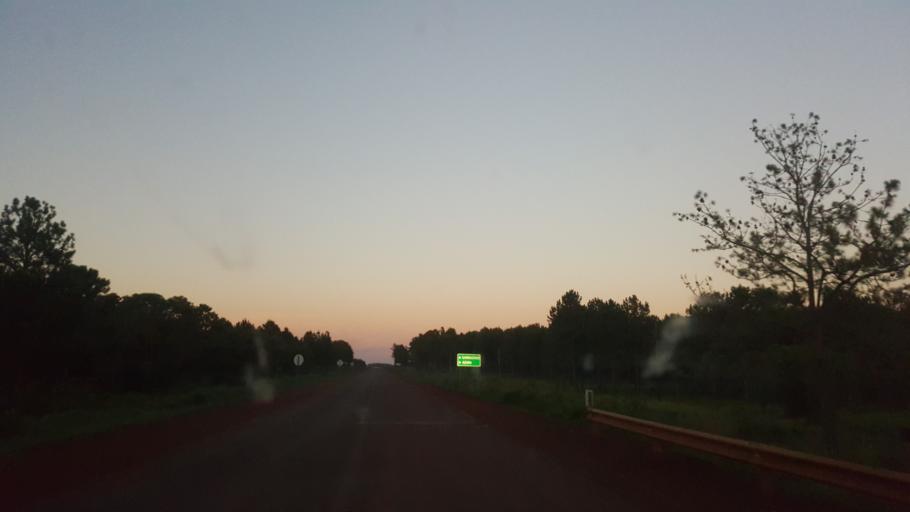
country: AR
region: Corrientes
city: Garruchos
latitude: -28.2250
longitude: -55.7998
